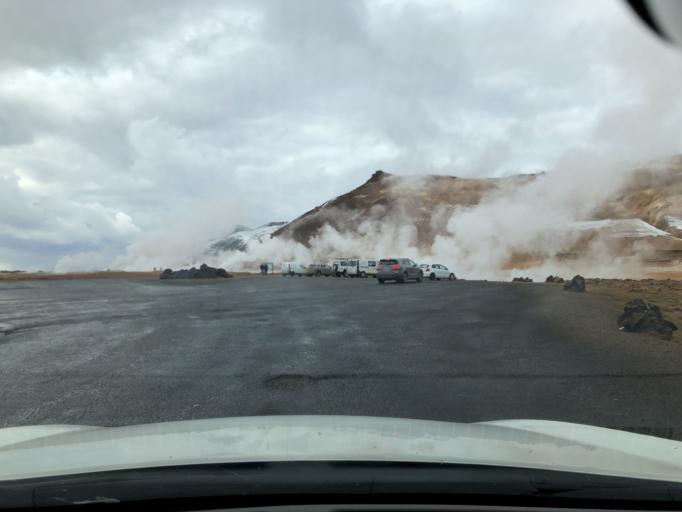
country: IS
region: Northeast
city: Laugar
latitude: 65.6421
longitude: -16.8064
